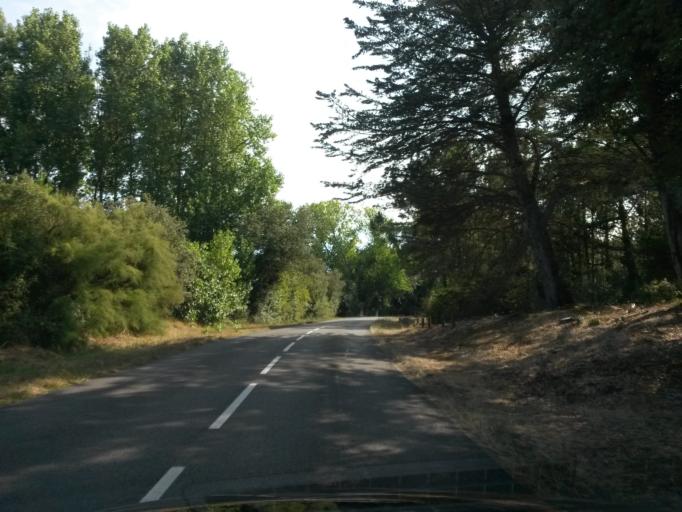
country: FR
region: Pays de la Loire
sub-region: Departement de la Vendee
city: Olonne-sur-Mer
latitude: 46.5360
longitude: -1.8127
